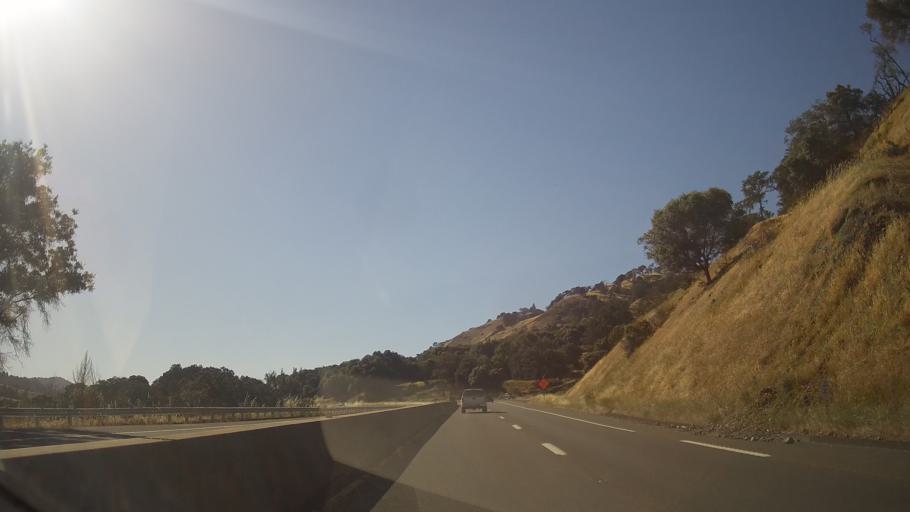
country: US
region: California
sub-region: Mendocino County
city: Redwood Valley
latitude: 39.2915
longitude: -123.2696
